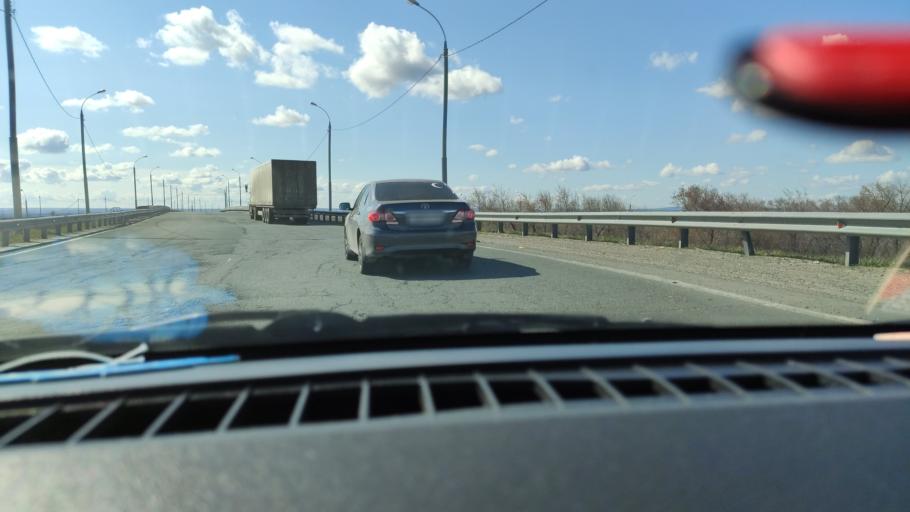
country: RU
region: Samara
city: Varlamovo
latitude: 53.1943
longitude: 48.2921
